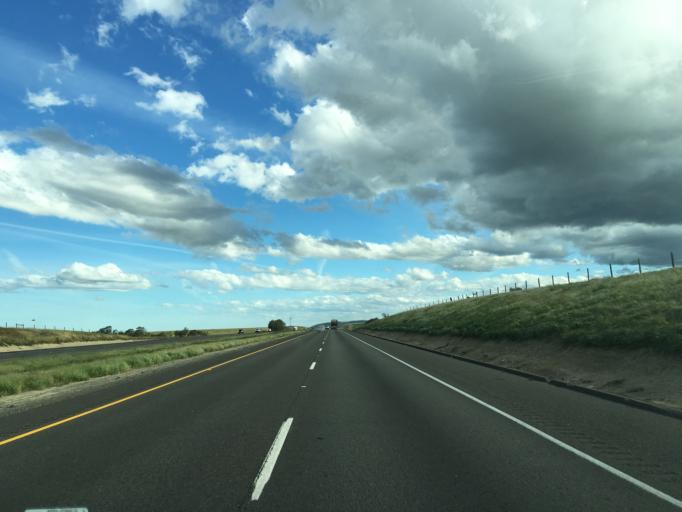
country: US
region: California
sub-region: Merced County
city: Los Banos
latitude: 37.0188
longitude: -120.9334
